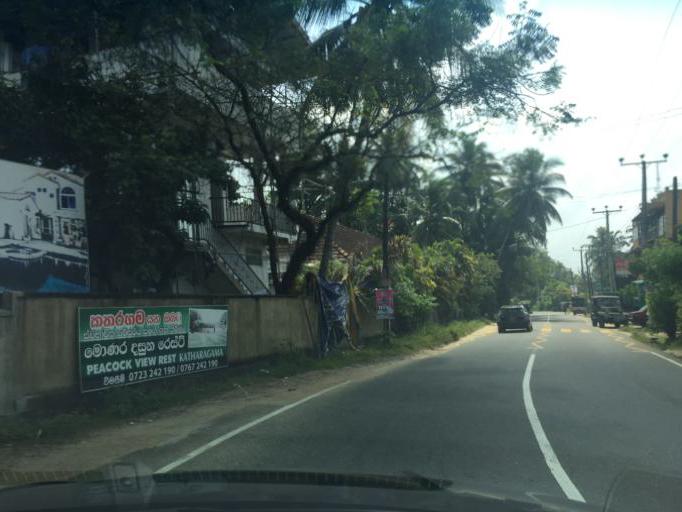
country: LK
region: Western
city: Horana South
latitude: 6.7196
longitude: 80.0608
